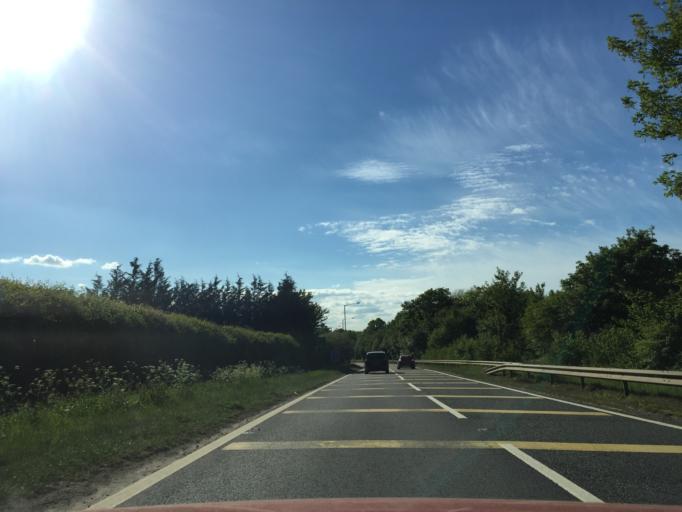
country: GB
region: England
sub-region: Warwickshire
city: Wolston
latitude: 52.3549
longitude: -1.3879
